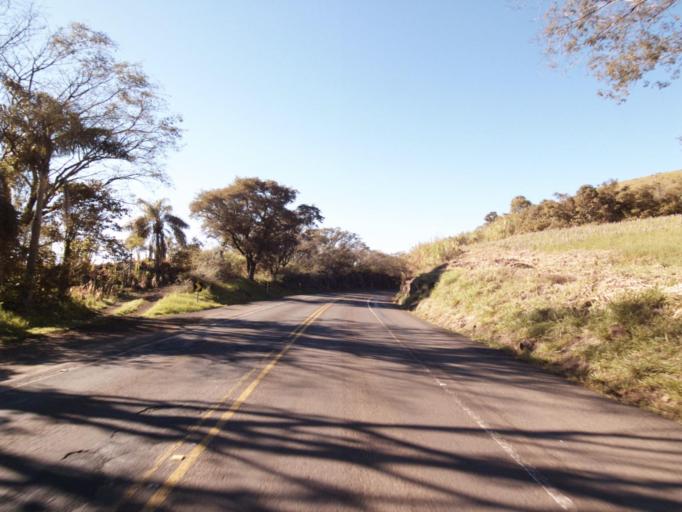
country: BR
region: Rio Grande do Sul
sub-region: Frederico Westphalen
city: Frederico Westphalen
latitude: -26.8041
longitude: -53.4430
